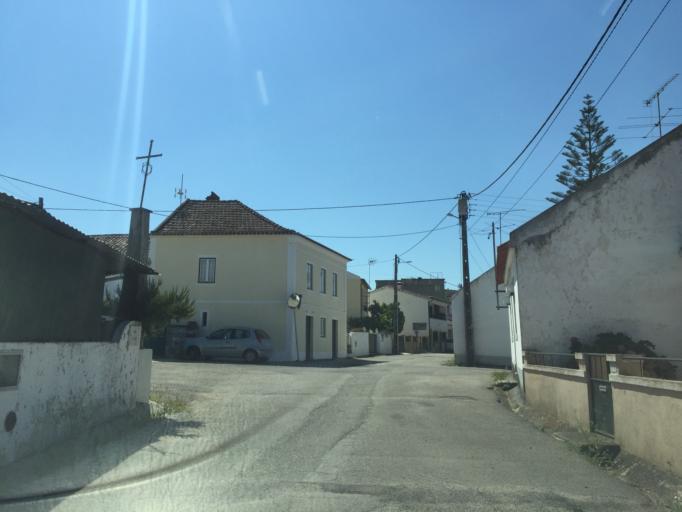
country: PT
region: Santarem
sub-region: Abrantes
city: Tramagal
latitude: 39.5447
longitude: -8.2739
